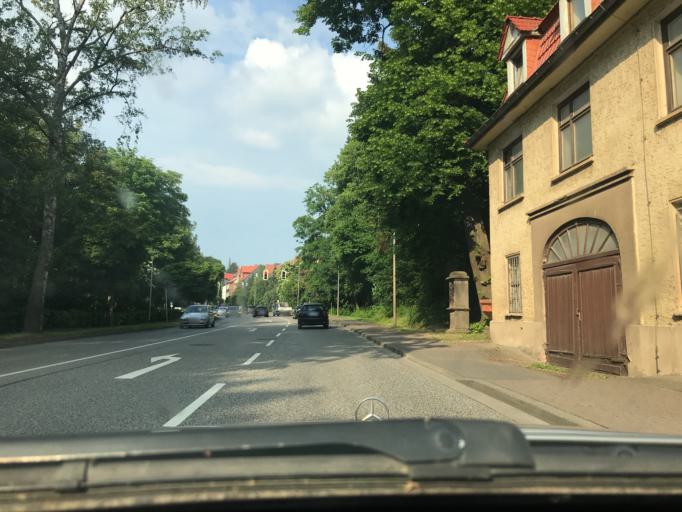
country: DE
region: Thuringia
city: Heilbad Heiligenstadt
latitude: 51.3739
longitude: 10.1241
